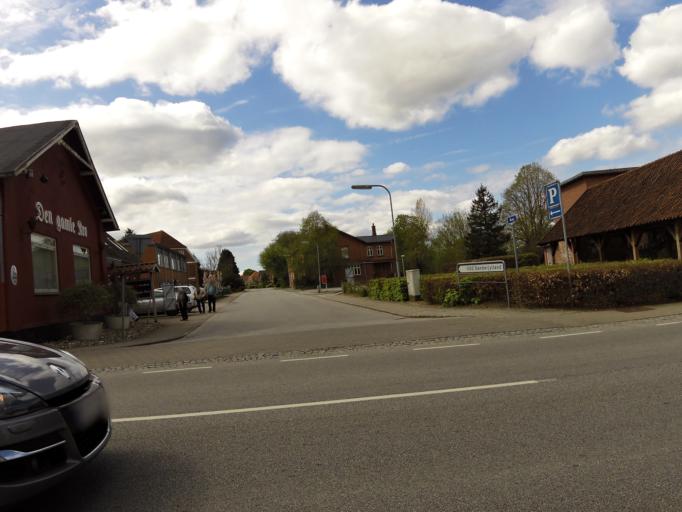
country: DK
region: South Denmark
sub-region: Haderslev Kommune
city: Gram
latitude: 55.2949
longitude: 9.0551
